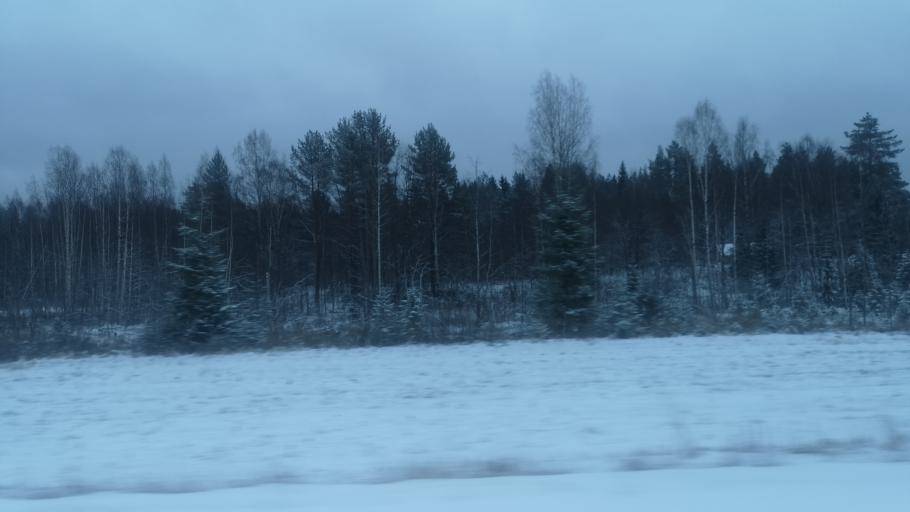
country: FI
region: Southern Savonia
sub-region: Savonlinna
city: Enonkoski
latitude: 62.0541
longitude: 28.7047
